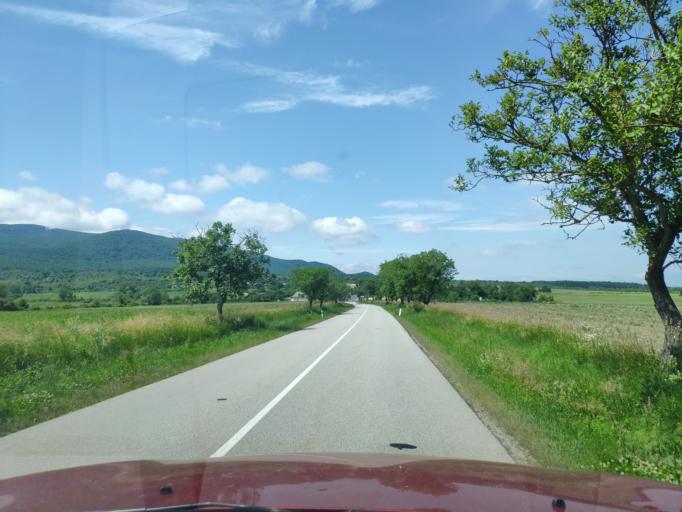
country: SK
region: Kosicky
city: Secovce
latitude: 48.7534
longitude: 21.6440
